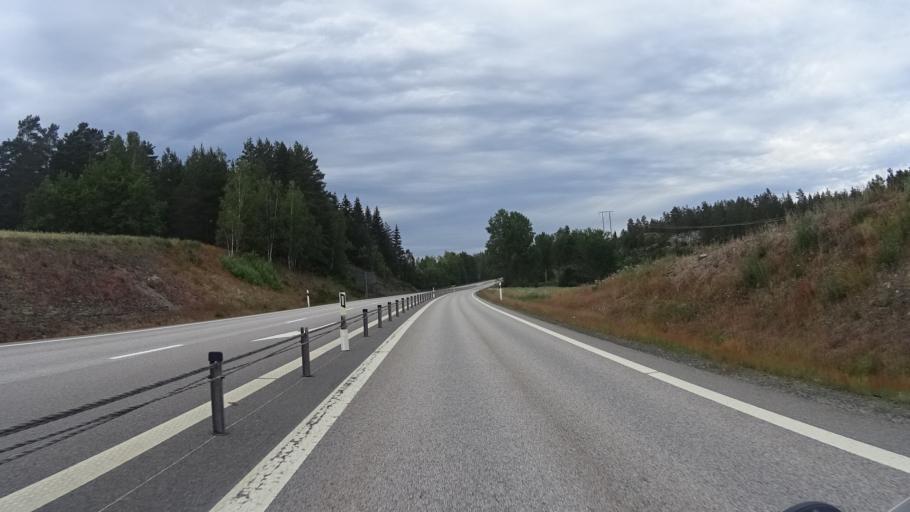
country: SE
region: OEstergoetland
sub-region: Valdemarsviks Kommun
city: Valdemarsvik
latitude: 58.0876
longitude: 16.5225
